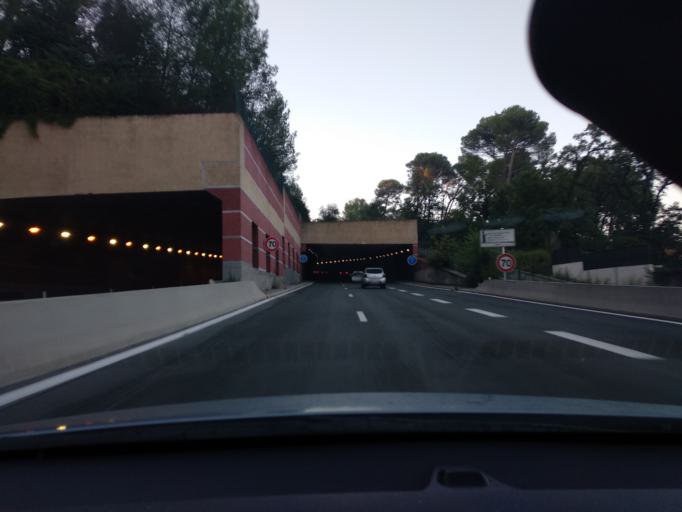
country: FR
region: Provence-Alpes-Cote d'Azur
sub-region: Departement des Alpes-Maritimes
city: Grasse
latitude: 43.6400
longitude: 6.9362
